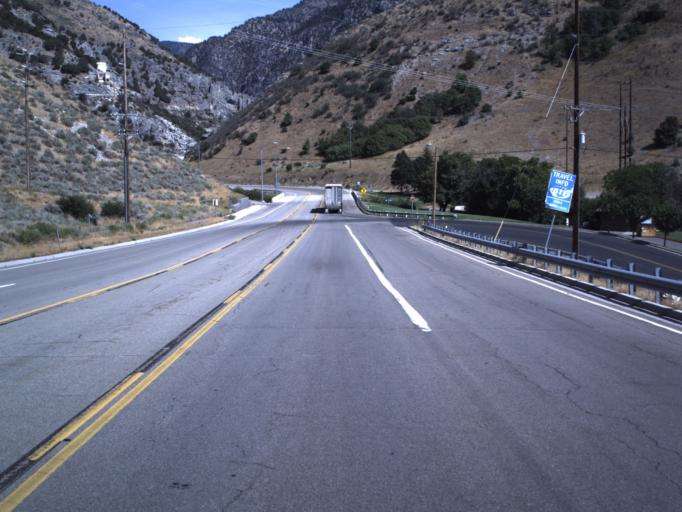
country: US
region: Utah
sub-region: Cache County
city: North Logan
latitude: 41.7432
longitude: -111.7891
